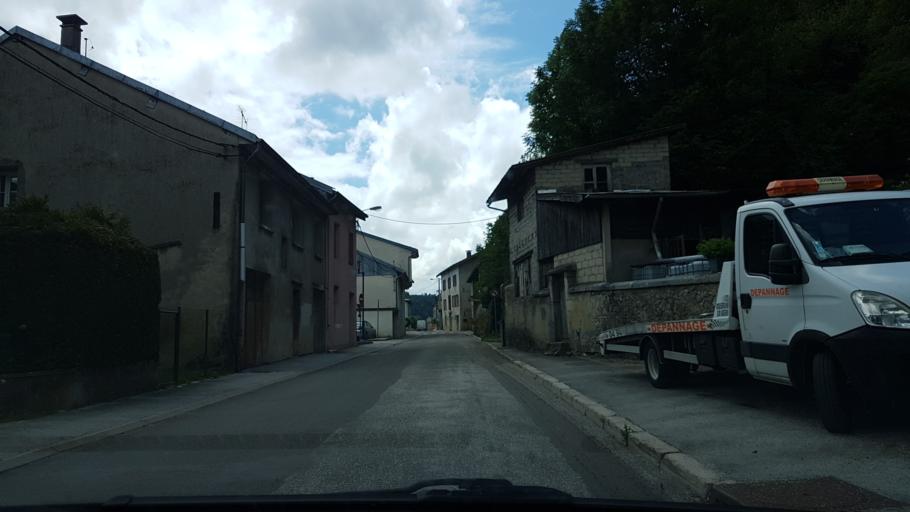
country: FR
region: Franche-Comte
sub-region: Departement du Jura
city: Moirans-en-Montagne
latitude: 46.4322
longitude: 5.7245
